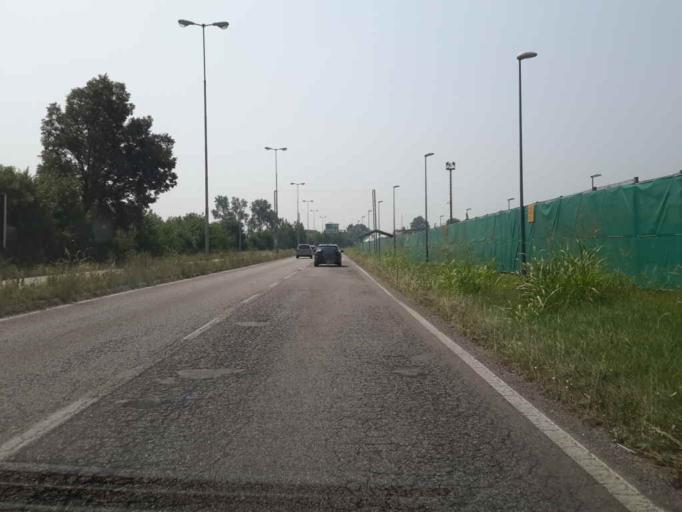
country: IT
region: Veneto
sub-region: Provincia di Vicenza
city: Villaggio Montegrappa
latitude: 45.5485
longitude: 11.5841
